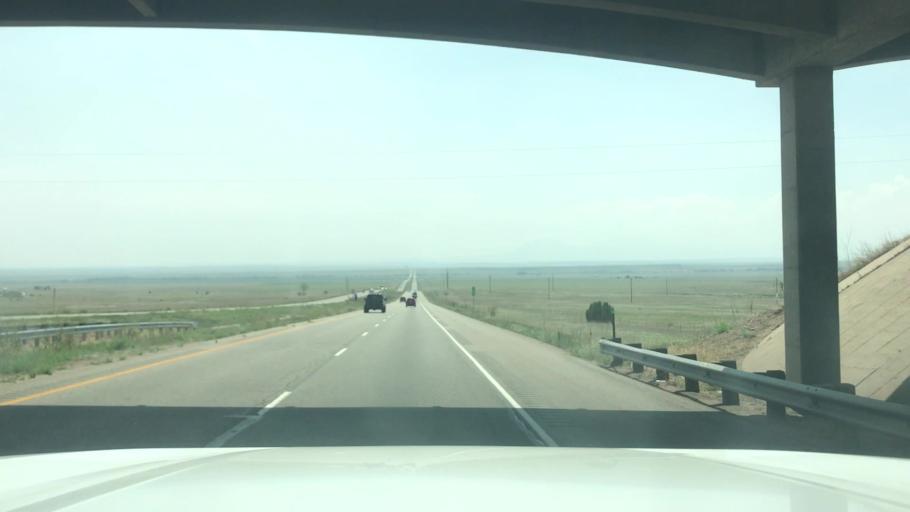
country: US
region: Colorado
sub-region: Pueblo County
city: Colorado City
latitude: 37.8944
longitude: -104.8293
